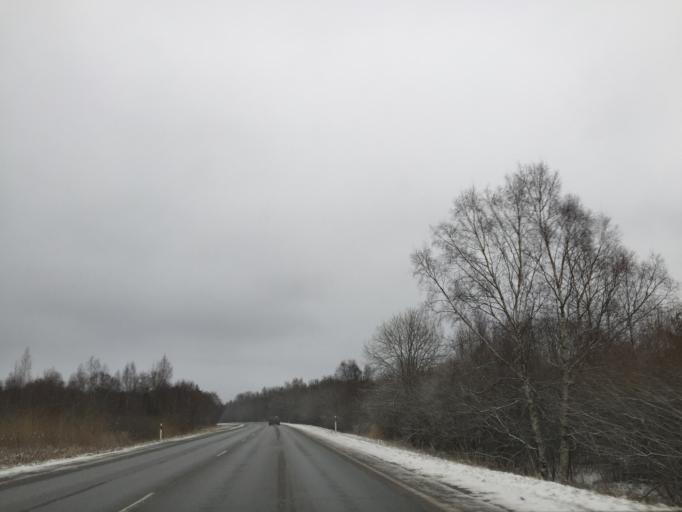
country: EE
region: Laeaene
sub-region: Lihula vald
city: Lihula
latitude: 58.5972
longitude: 23.5490
